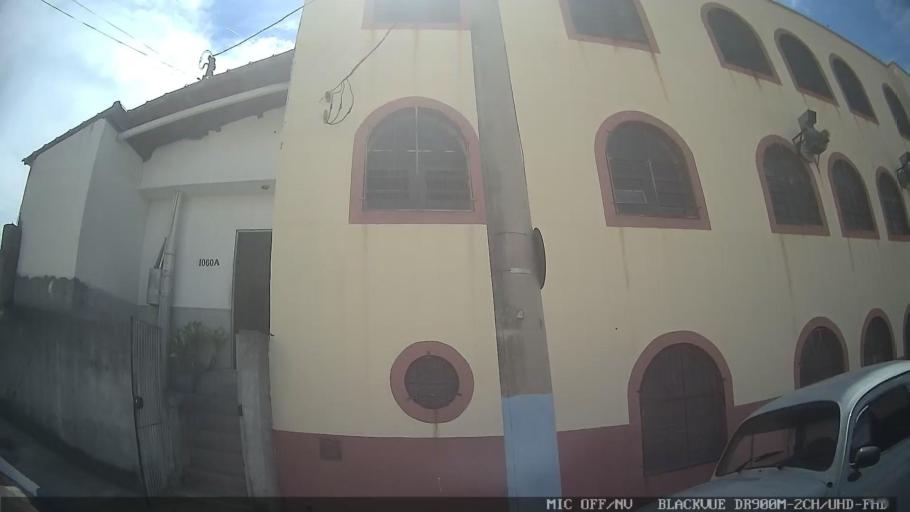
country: BR
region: Sao Paulo
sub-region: Conchas
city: Conchas
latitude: -23.0165
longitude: -48.0105
